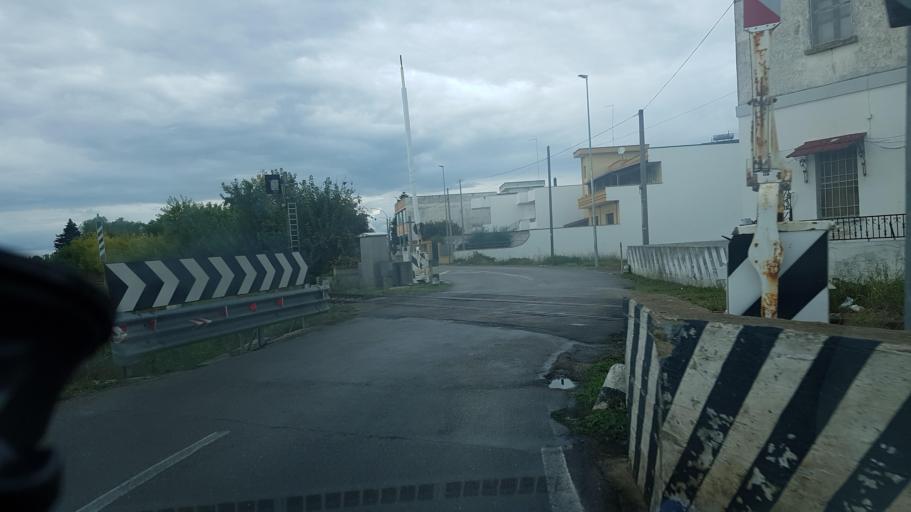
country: IT
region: Apulia
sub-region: Provincia di Lecce
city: Guagnano
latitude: 40.3938
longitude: 17.9560
